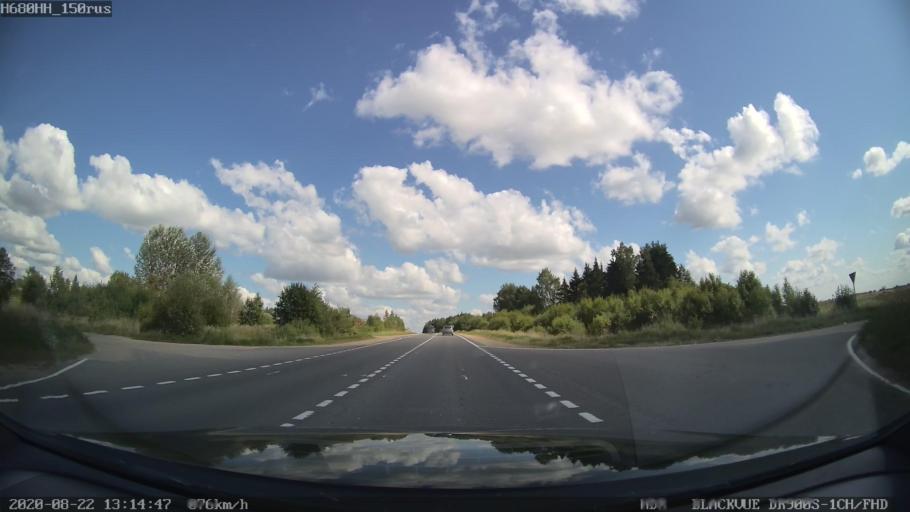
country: RU
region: Tverskaya
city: Bezhetsk
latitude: 57.7553
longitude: 36.6109
